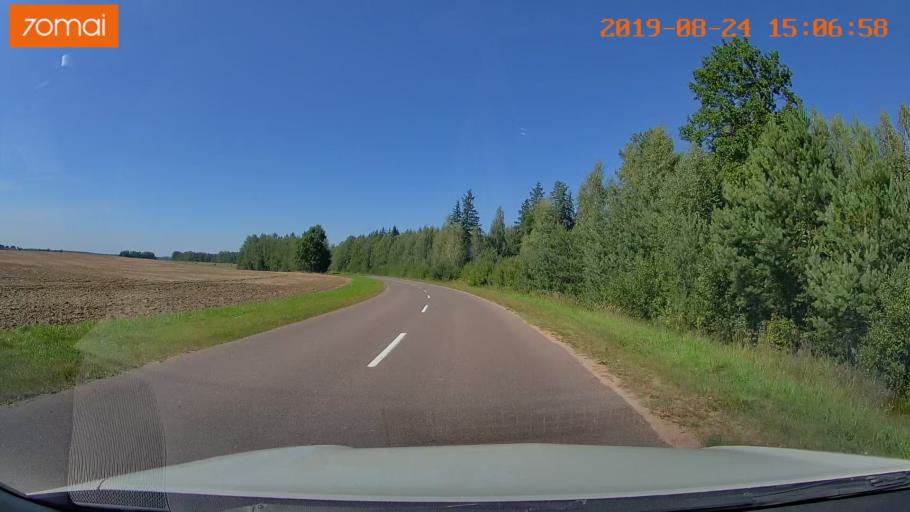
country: BY
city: Michanovichi
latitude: 53.6053
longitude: 27.6784
